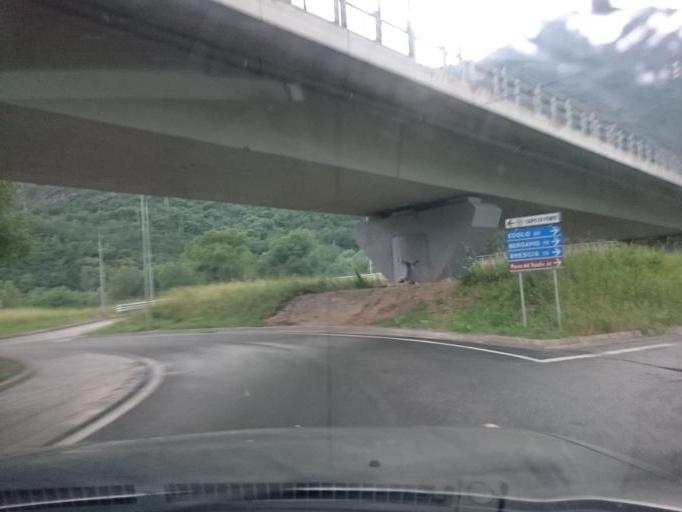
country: IT
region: Lombardy
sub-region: Provincia di Brescia
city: Capo di Ponte
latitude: 46.0367
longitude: 10.3481
